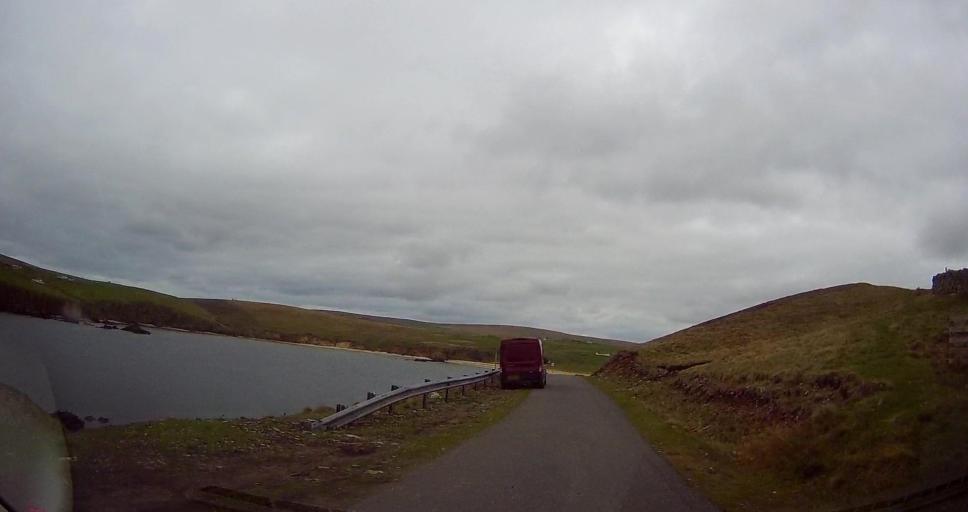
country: GB
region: Scotland
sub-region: Shetland Islands
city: Shetland
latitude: 60.8120
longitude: -0.8763
